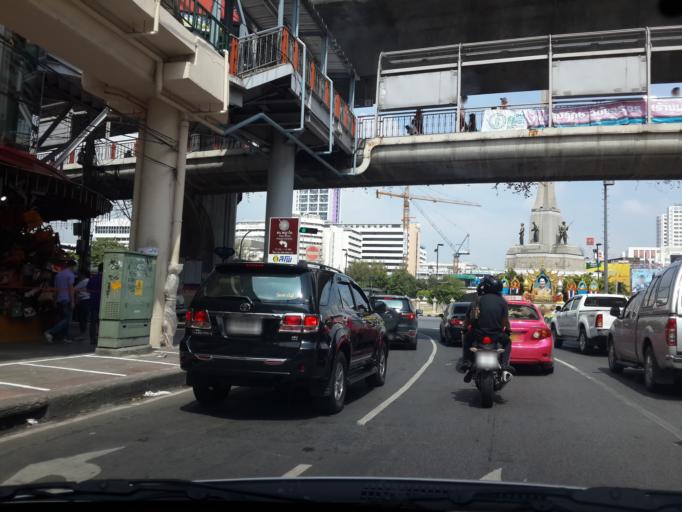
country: TH
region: Bangkok
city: Ratchathewi
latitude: 13.7645
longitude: 100.5393
